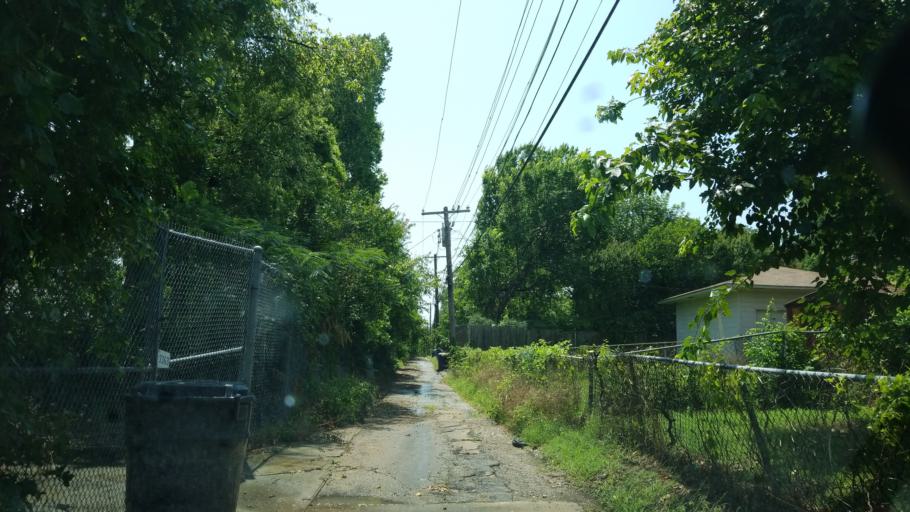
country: US
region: Texas
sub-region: Dallas County
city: Farmers Branch
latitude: 32.8776
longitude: -96.8650
